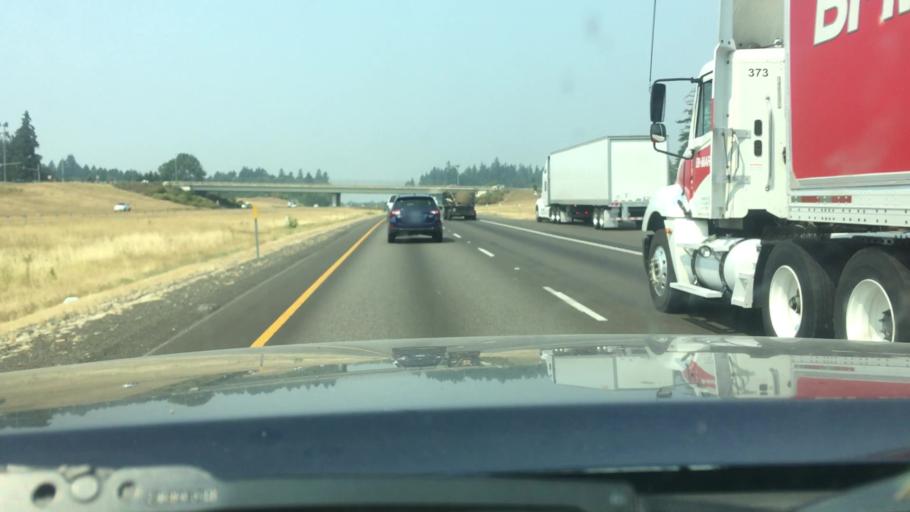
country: US
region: Oregon
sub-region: Clackamas County
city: Stafford
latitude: 45.3693
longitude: -122.7018
